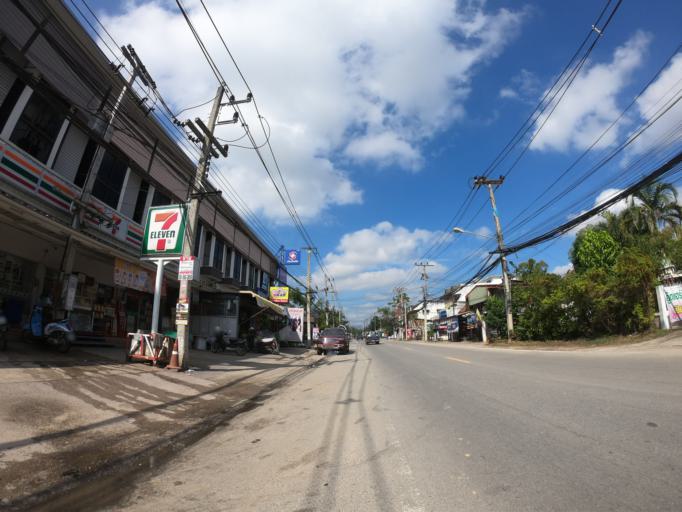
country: TH
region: Chiang Mai
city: San Sai
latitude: 18.8451
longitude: 99.0436
